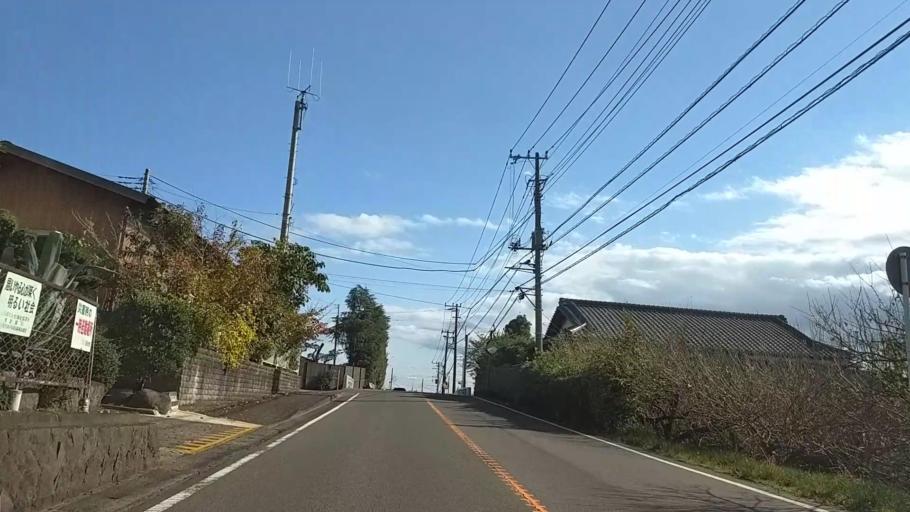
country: JP
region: Kanagawa
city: Odawara
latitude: 35.3147
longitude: 139.1744
